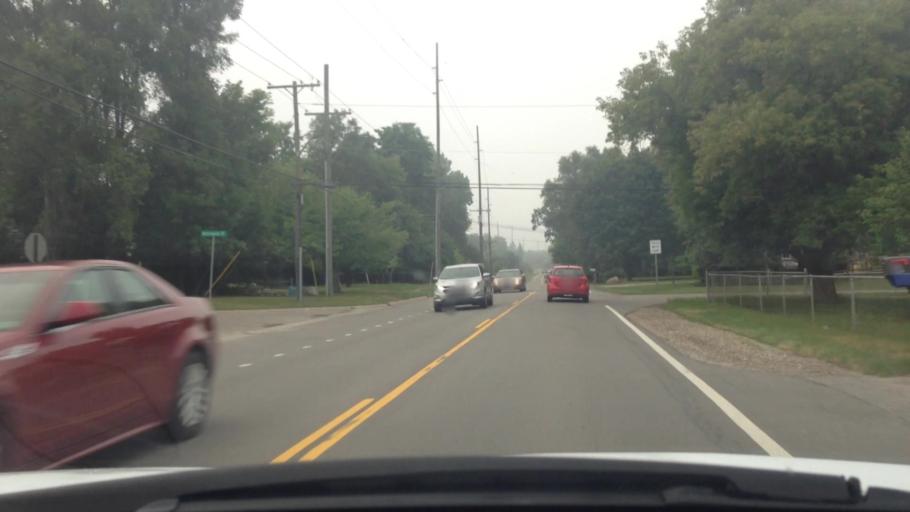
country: US
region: Michigan
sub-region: Oakland County
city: Waterford
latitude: 42.7013
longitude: -83.3488
